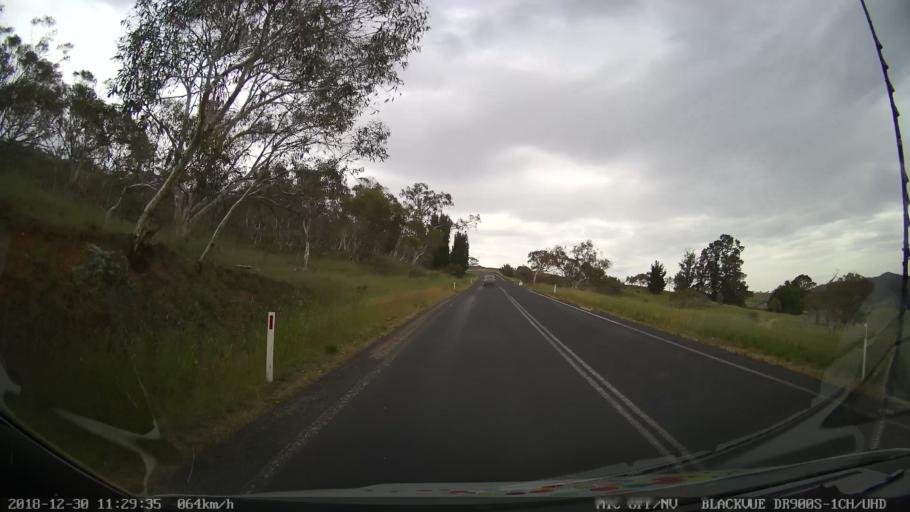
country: AU
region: New South Wales
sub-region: Snowy River
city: Jindabyne
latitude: -36.4493
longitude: 148.6096
